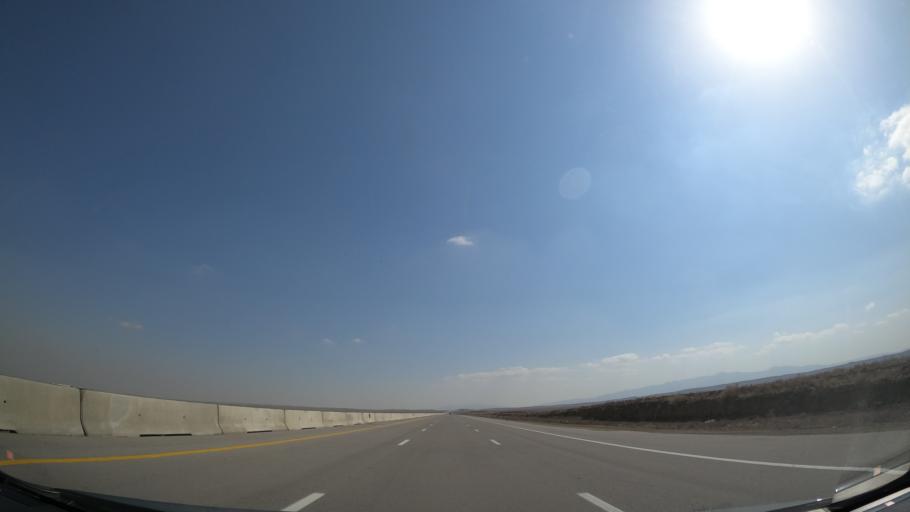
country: IR
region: Alborz
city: Nazarabad
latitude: 35.8265
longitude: 50.5059
